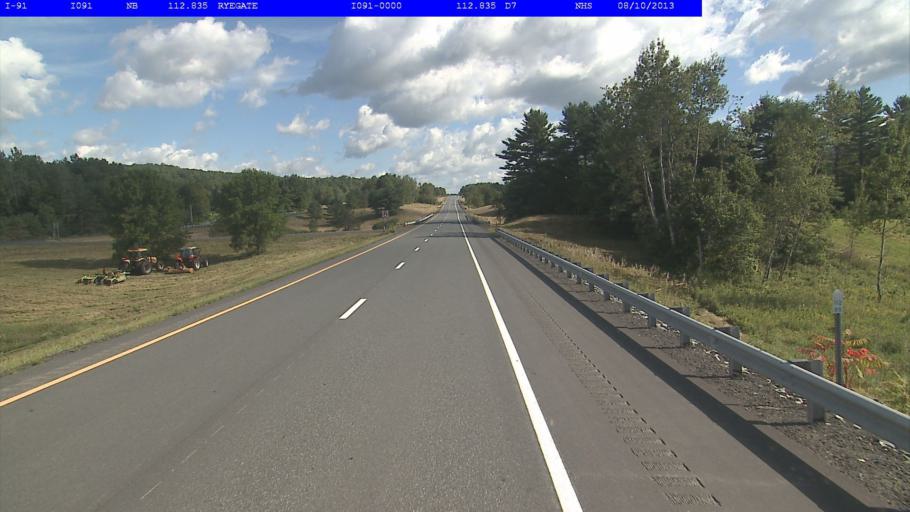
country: US
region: New Hampshire
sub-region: Grafton County
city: Woodsville
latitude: 44.1938
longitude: -72.0723
